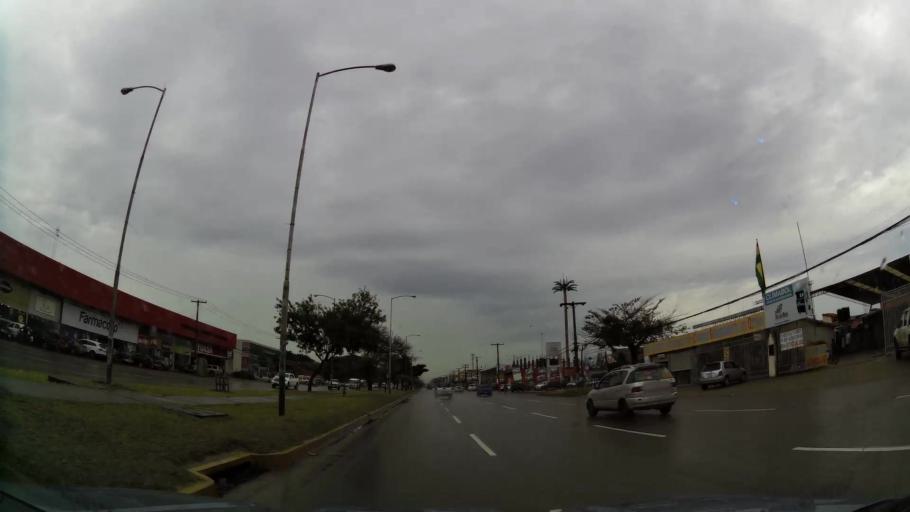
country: BO
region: Santa Cruz
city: Santa Cruz de la Sierra
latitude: -17.8081
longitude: -63.2040
